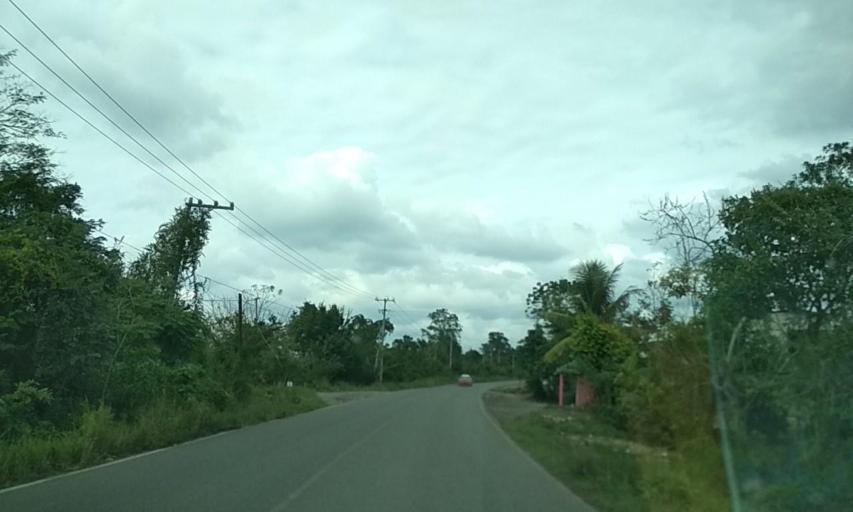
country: MX
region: Veracruz
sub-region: Papantla
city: El Chote
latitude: 20.3820
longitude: -97.3366
